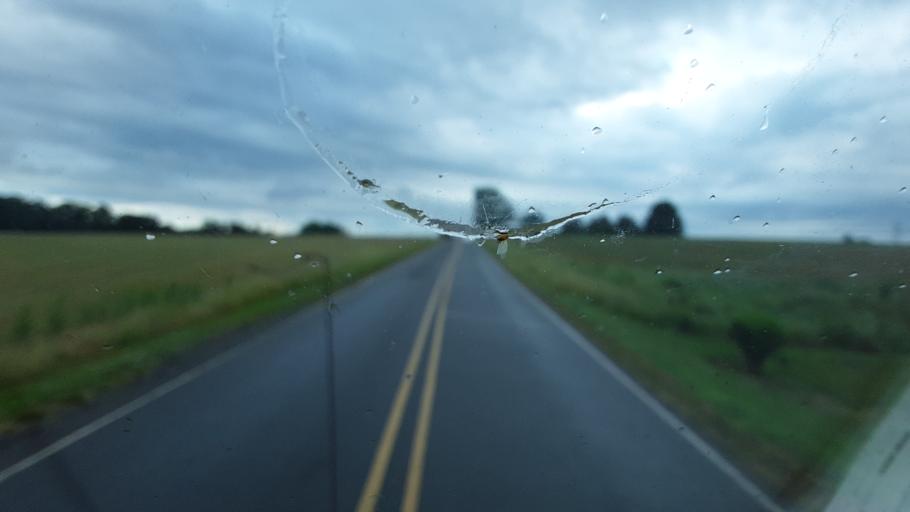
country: US
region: North Carolina
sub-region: Yadkin County
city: Jonesville
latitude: 36.0590
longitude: -80.8311
